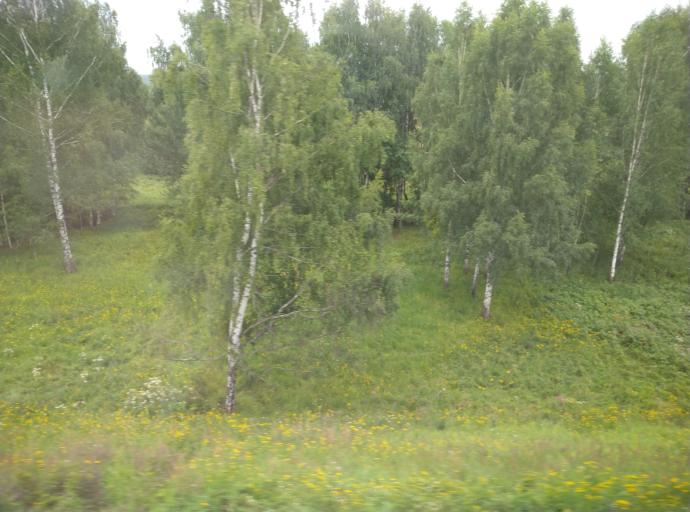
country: RU
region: Kostroma
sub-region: Kostromskoy Rayon
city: Kostroma
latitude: 57.7342
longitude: 40.9384
